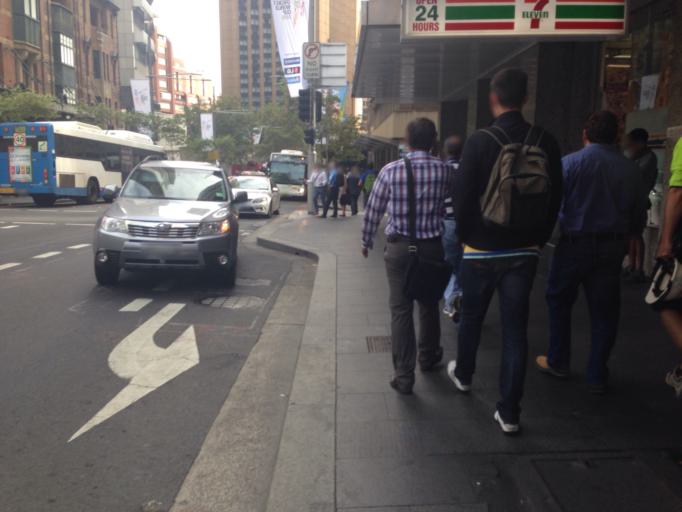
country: AU
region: New South Wales
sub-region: City of Sydney
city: Sydney
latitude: -33.8633
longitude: 151.2076
